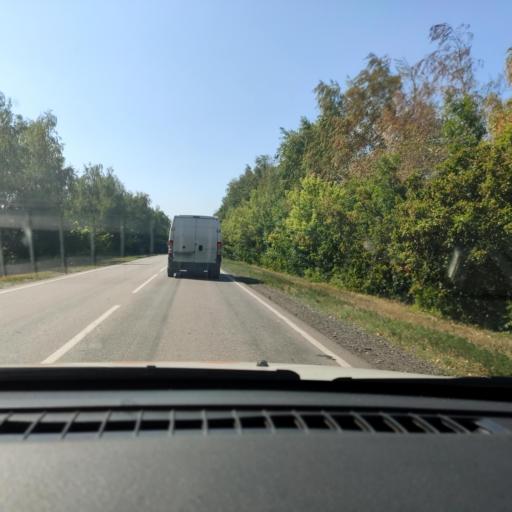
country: RU
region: Voronezj
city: Ostrogozhsk
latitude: 50.8027
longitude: 39.3166
